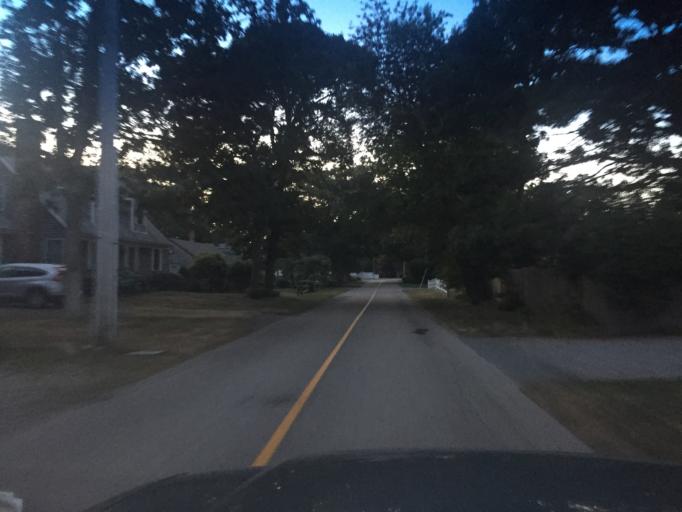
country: US
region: Massachusetts
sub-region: Barnstable County
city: Teaticket
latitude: 41.5489
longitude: -70.5982
